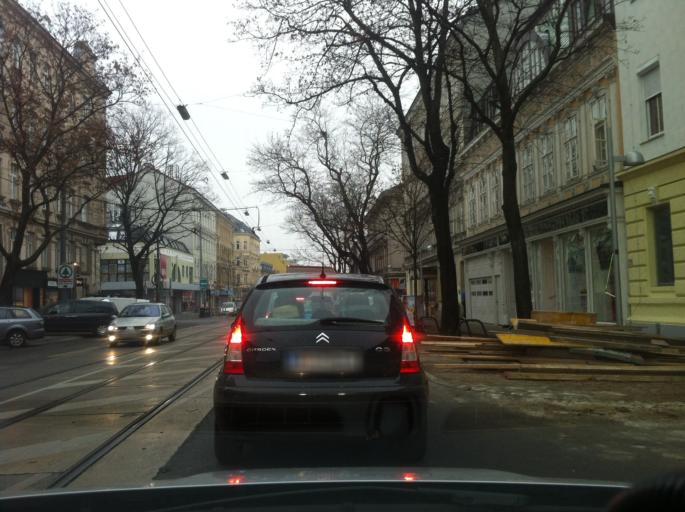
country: AT
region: Vienna
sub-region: Wien Stadt
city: Vienna
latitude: 48.1936
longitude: 16.3096
